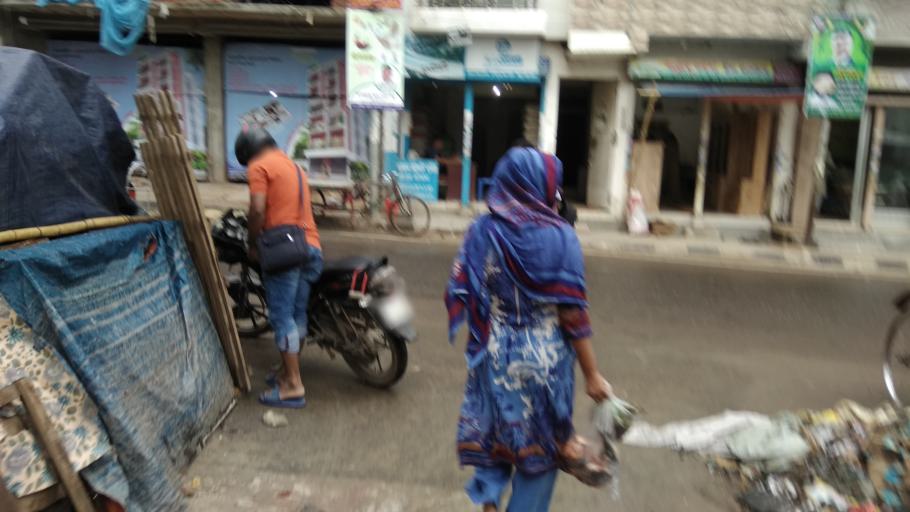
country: BD
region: Dhaka
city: Tungi
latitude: 23.8248
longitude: 90.3695
